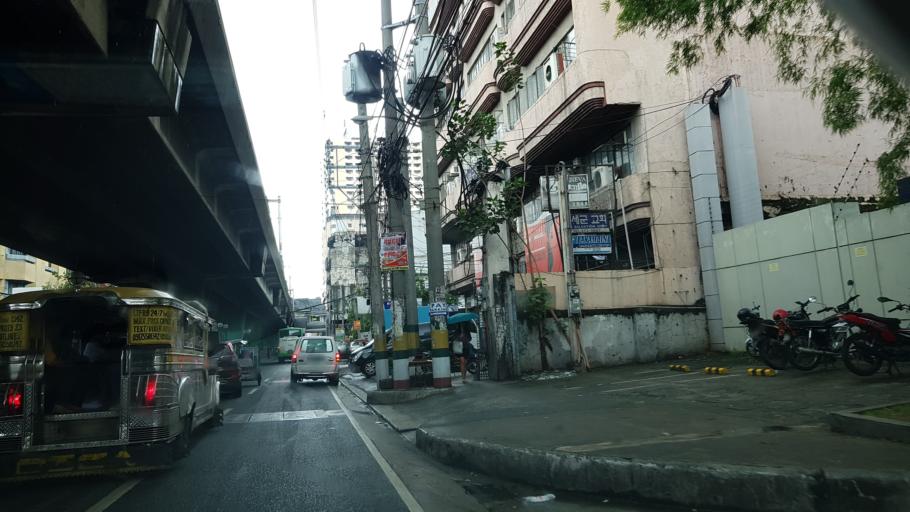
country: PH
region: Metro Manila
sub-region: Makati City
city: Makati City
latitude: 14.5567
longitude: 120.9965
